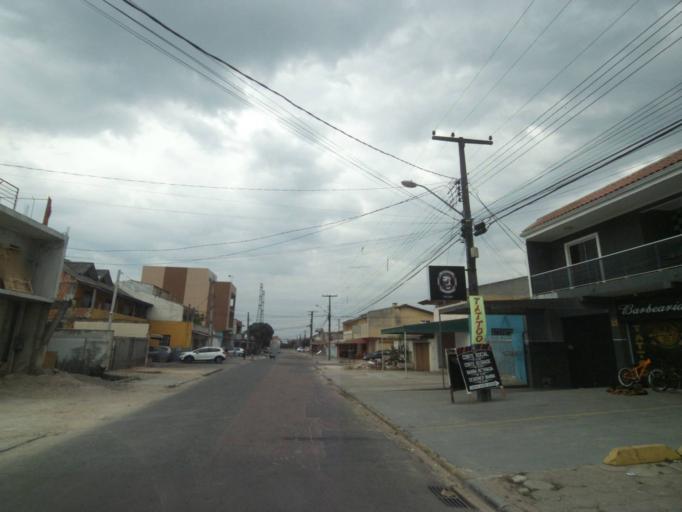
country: BR
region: Parana
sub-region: Pinhais
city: Pinhais
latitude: -25.4843
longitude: -49.1959
